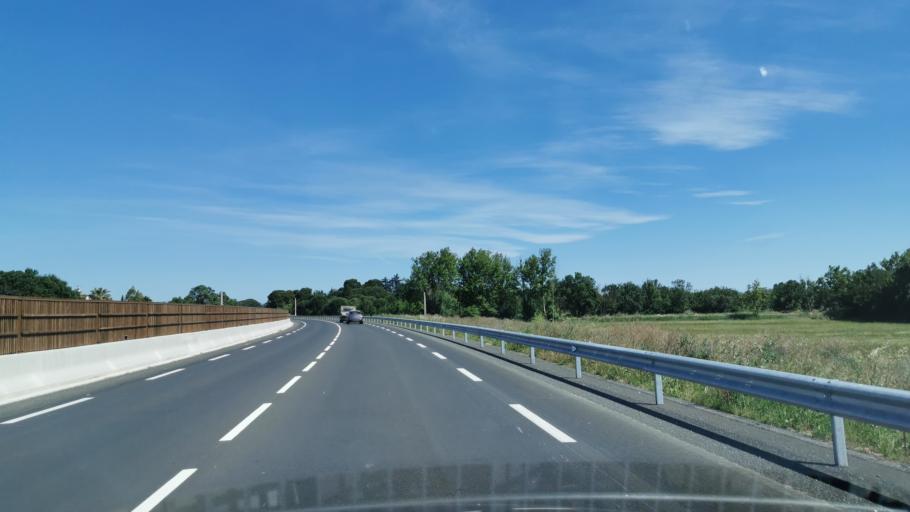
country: FR
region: Languedoc-Roussillon
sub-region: Departement de l'Aude
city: Narbonne
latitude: 43.1882
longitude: 3.0328
